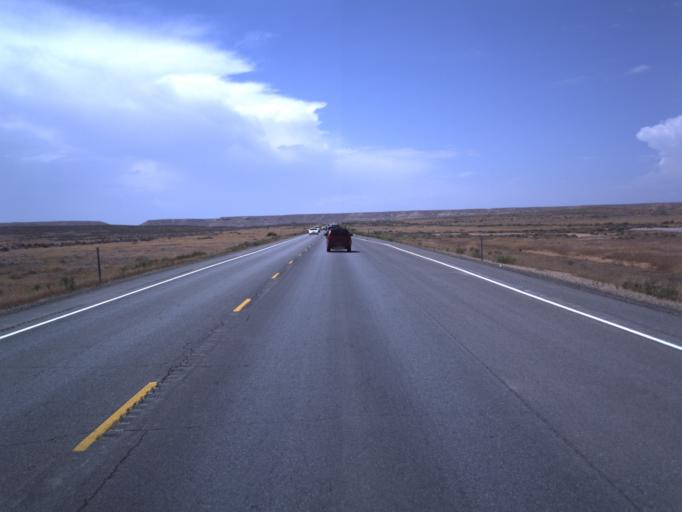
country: US
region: Utah
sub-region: Uintah County
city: Maeser
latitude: 40.3318
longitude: -109.6550
